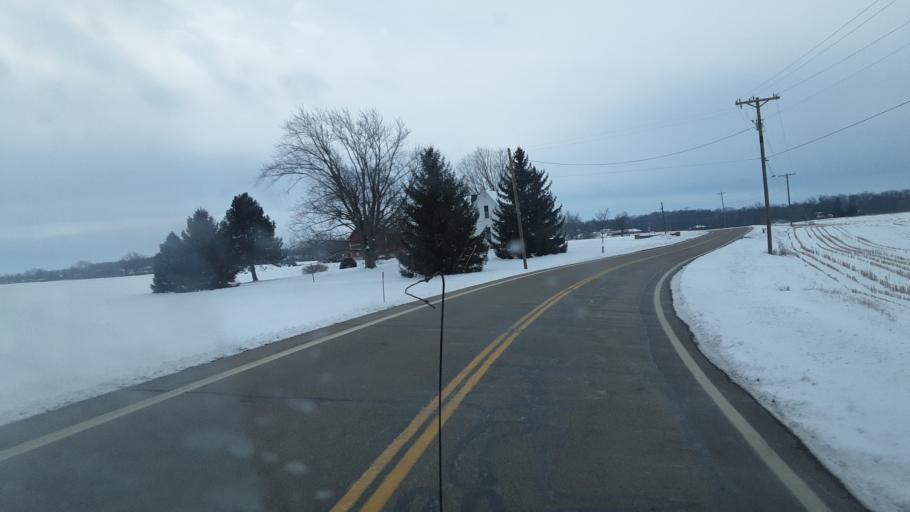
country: US
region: Ohio
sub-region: Champaign County
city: Mechanicsburg
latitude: 40.0453
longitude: -83.5338
